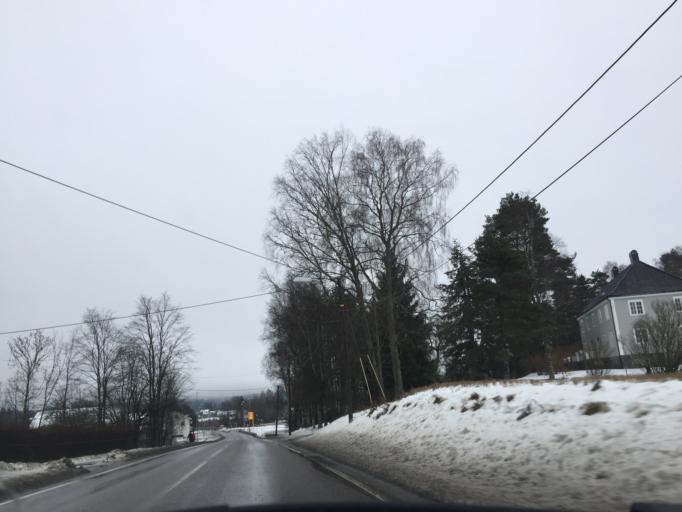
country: NO
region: Akershus
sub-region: Vestby
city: Vestby
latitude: 59.6071
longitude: 10.7430
